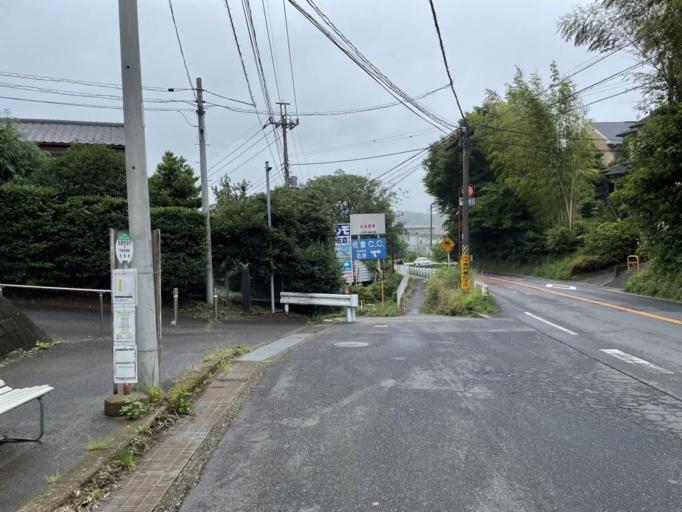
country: JP
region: Chiba
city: Sakura
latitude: 35.7237
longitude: 140.2251
